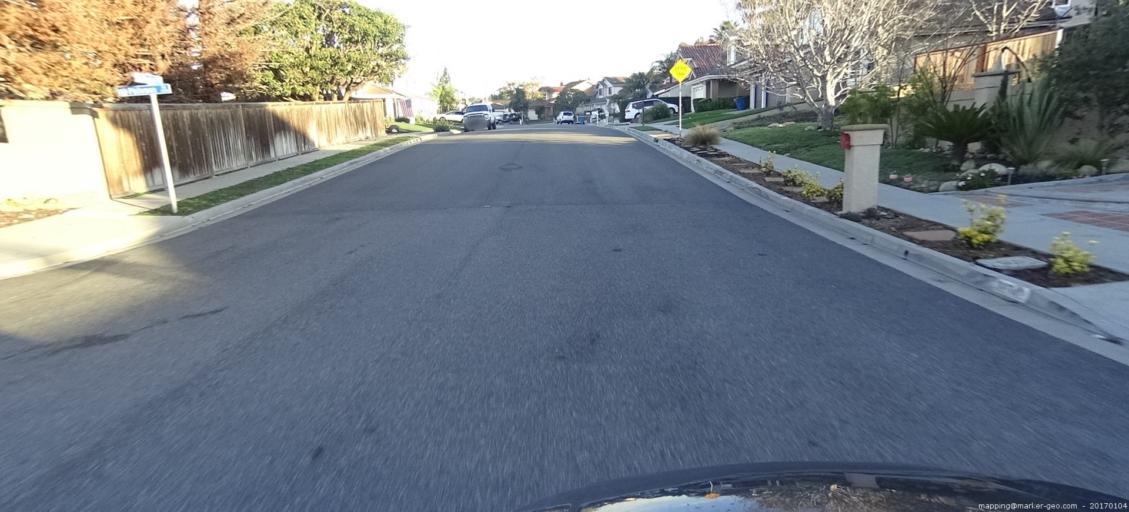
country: US
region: California
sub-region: Orange County
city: Dana Point
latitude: 33.4872
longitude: -117.7028
